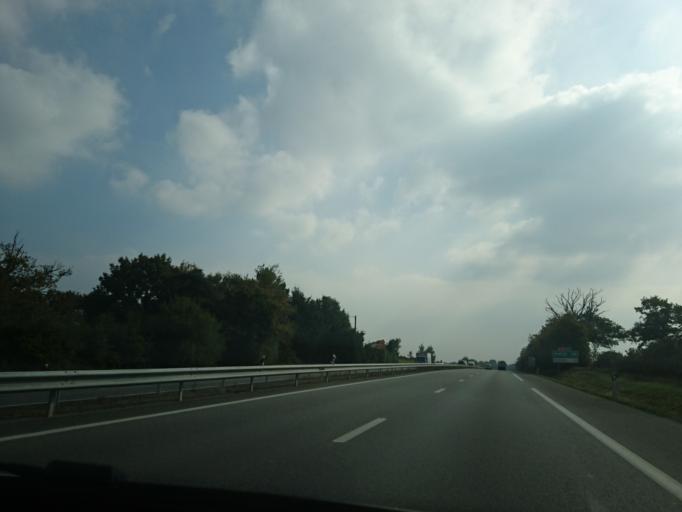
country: FR
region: Brittany
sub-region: Departement d'Ille-et-Vilaine
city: Grand-Fougeray
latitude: 47.7369
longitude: -1.7130
